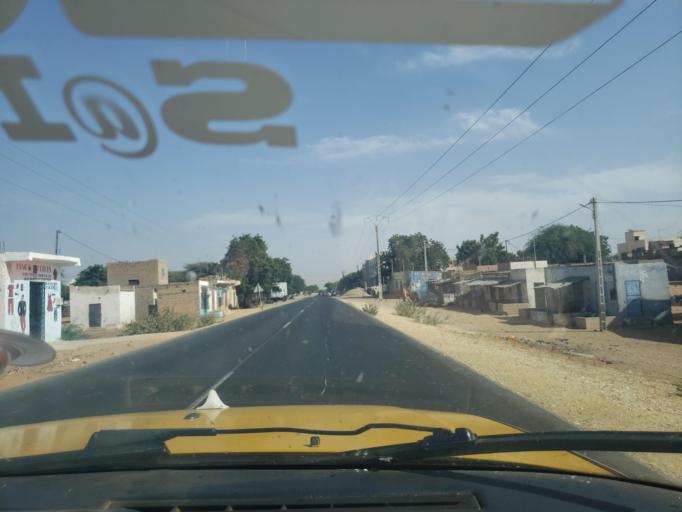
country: SN
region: Saint-Louis
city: Saint-Louis
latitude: 15.9291
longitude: -16.3261
